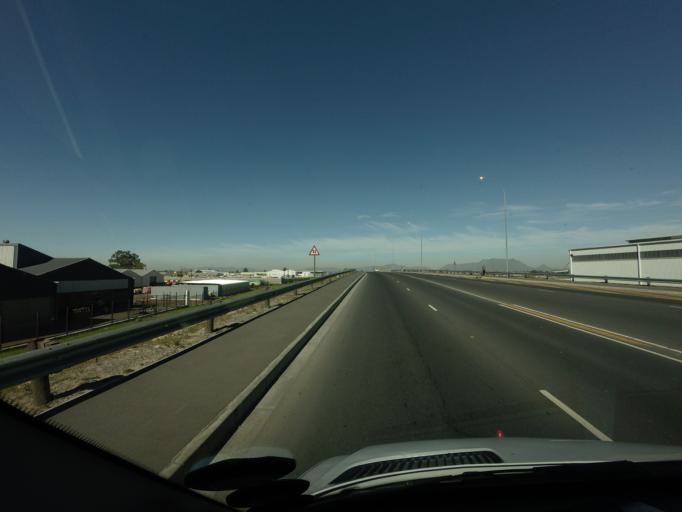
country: ZA
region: Western Cape
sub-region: City of Cape Town
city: Kraaifontein
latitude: -33.9523
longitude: 18.6946
